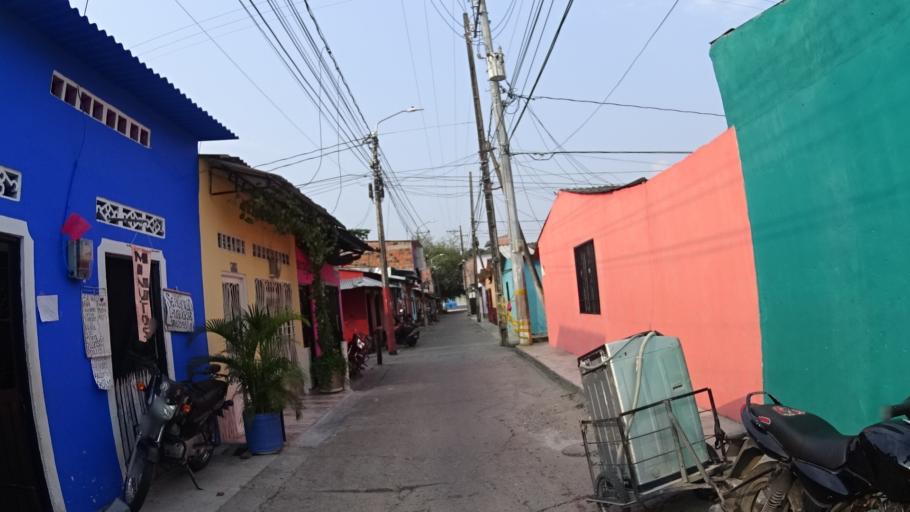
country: CO
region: Cundinamarca
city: Puerto Salgar
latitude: 5.4781
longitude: -74.6761
